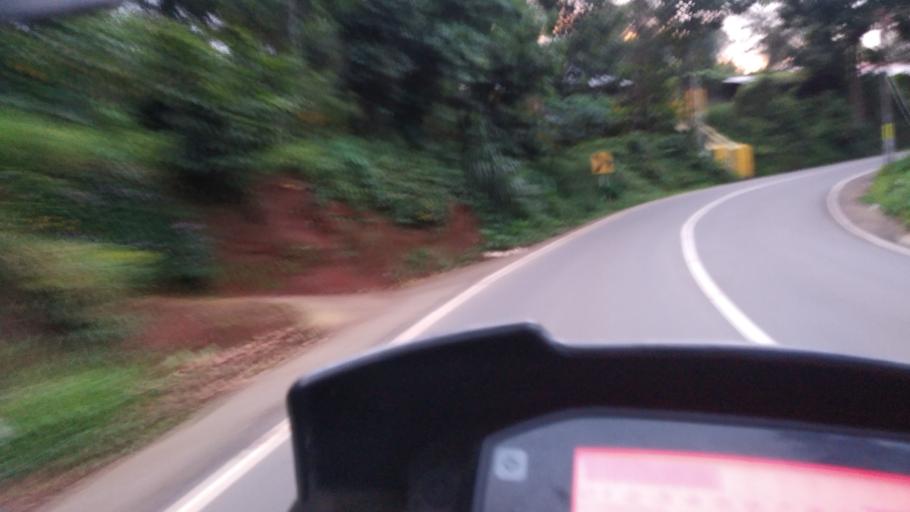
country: IN
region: Kerala
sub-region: Idukki
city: Munnar
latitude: 9.9684
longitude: 77.1196
